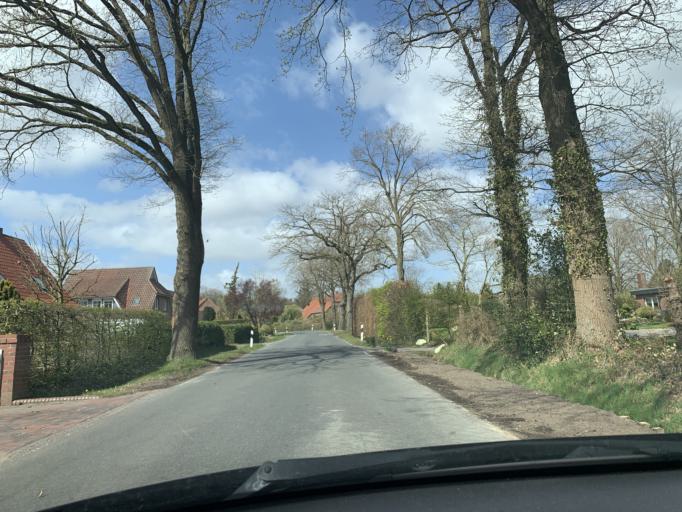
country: DE
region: Lower Saxony
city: Westerstede
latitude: 53.3062
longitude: 7.9405
